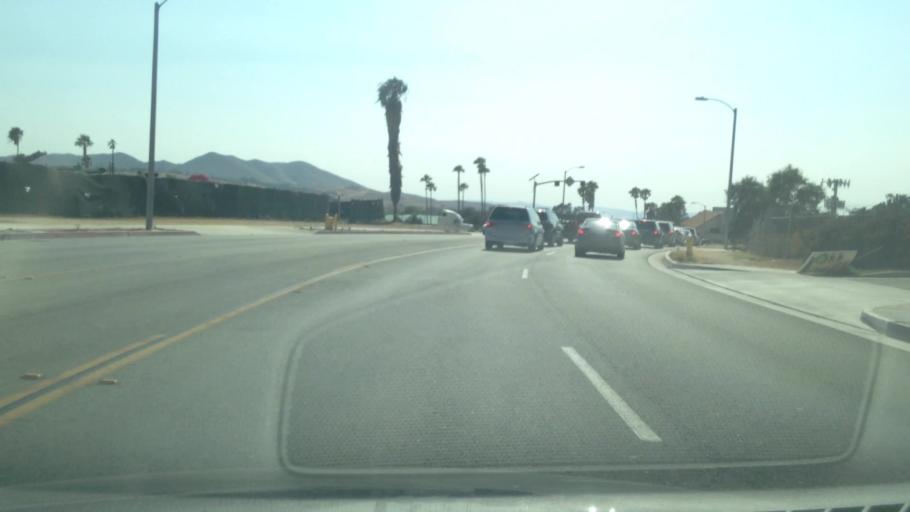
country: US
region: California
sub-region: Riverside County
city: Pedley
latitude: 33.9681
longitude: -117.4633
